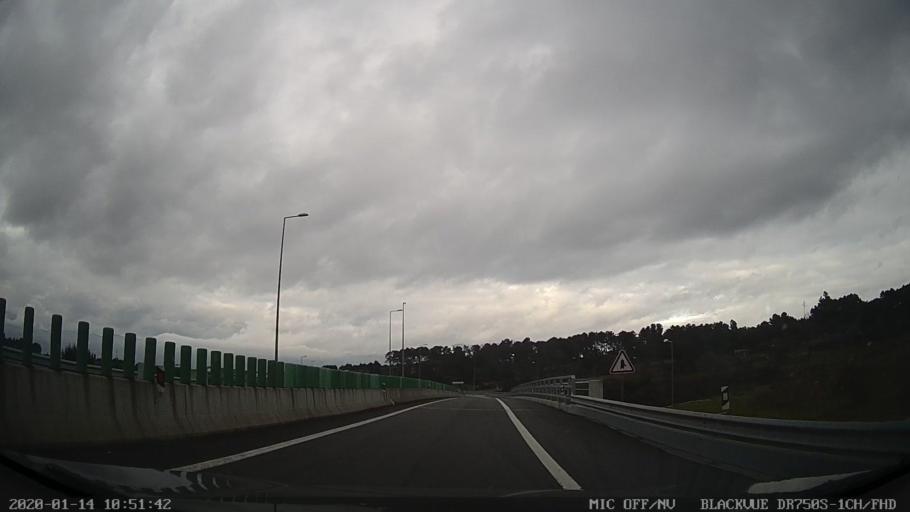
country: PT
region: Vila Real
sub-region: Vila Real
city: Vila Real
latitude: 41.2934
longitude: -7.6887
